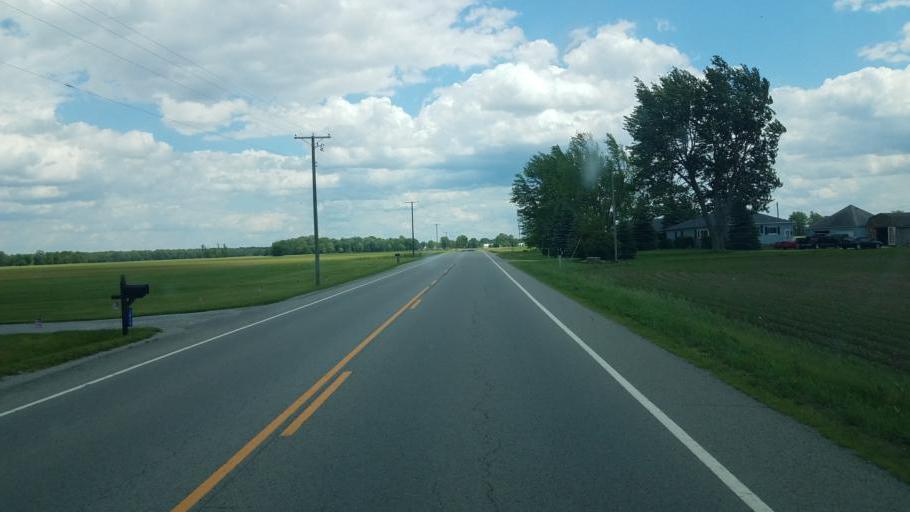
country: US
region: Ohio
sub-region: Crawford County
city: Galion
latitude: 40.8120
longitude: -82.8356
